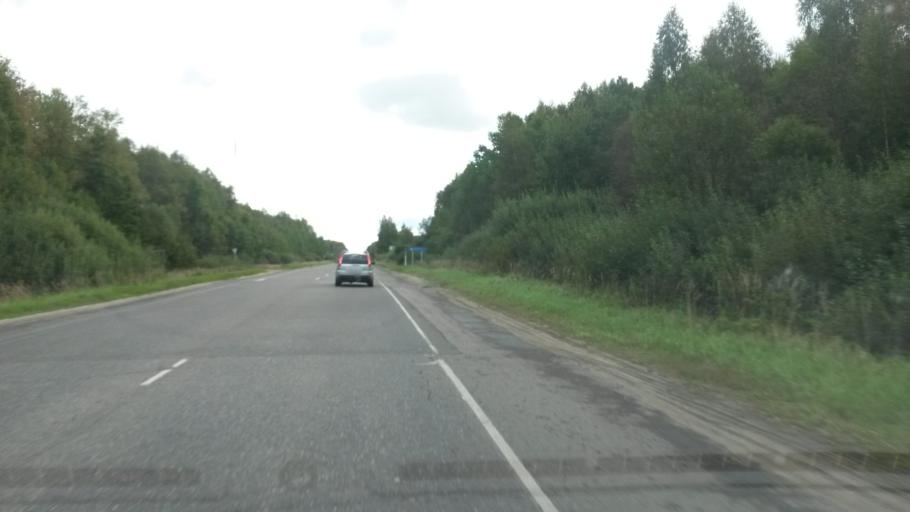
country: RU
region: Ivanovo
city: Rodniki
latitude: 57.0882
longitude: 41.6772
